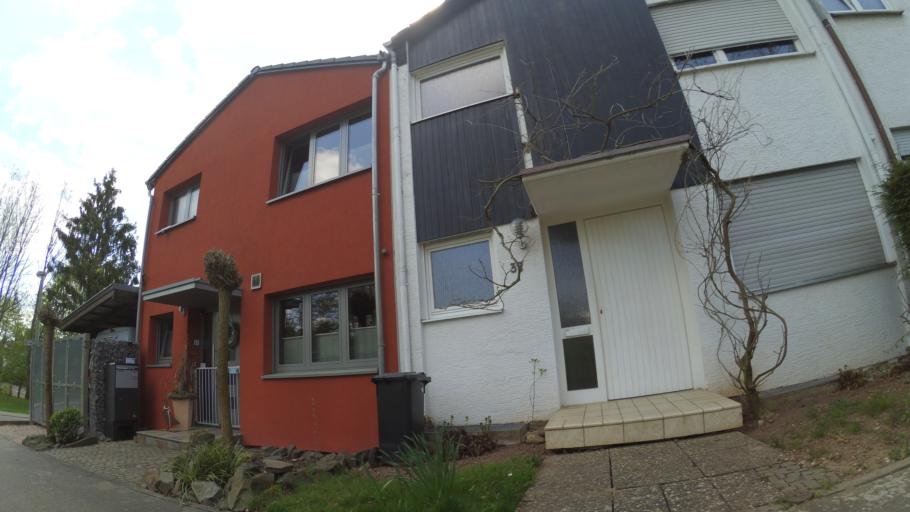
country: DE
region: Saarland
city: Riegelsberg
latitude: 49.3155
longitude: 6.9349
